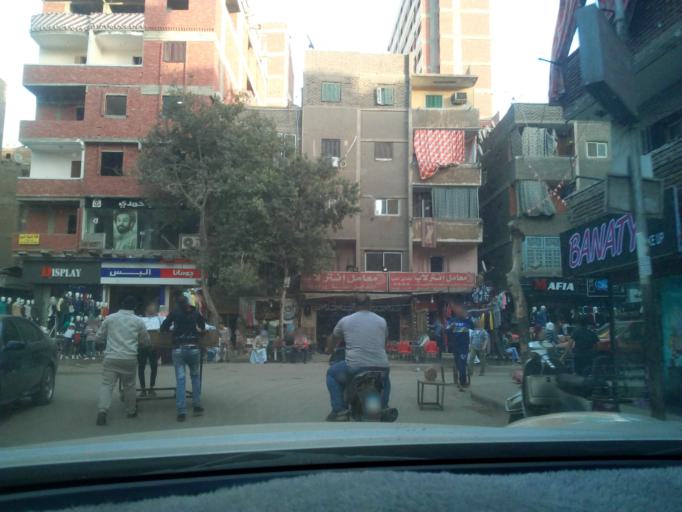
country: EG
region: Muhafazat al Qalyubiyah
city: Al Khankah
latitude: 30.1298
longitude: 31.3462
